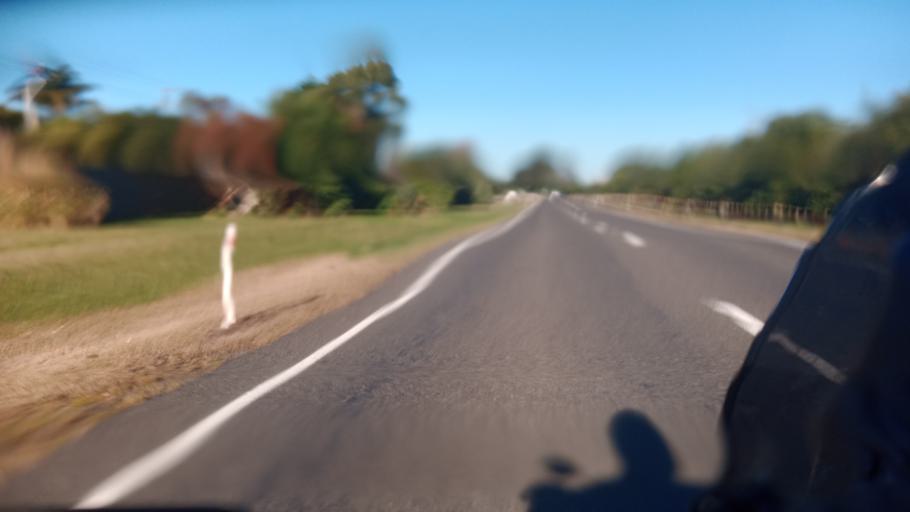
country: NZ
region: Hawke's Bay
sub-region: Napier City
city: Napier
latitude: -39.3713
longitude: 176.8956
